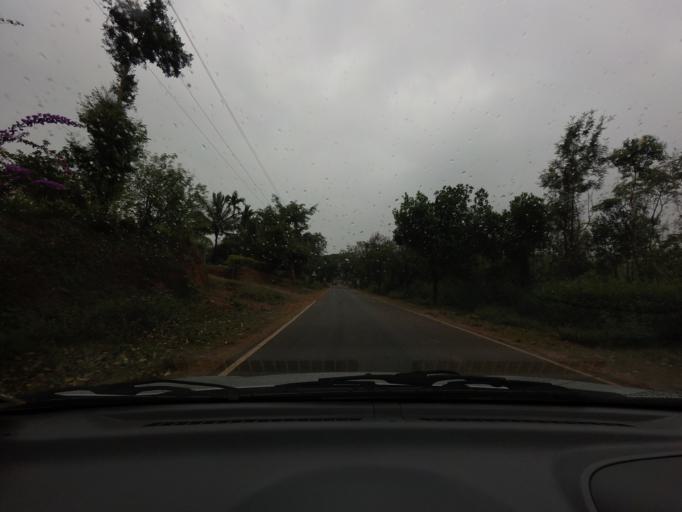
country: IN
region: Karnataka
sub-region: Hassan
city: Sakleshpur
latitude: 12.9914
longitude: 75.7095
